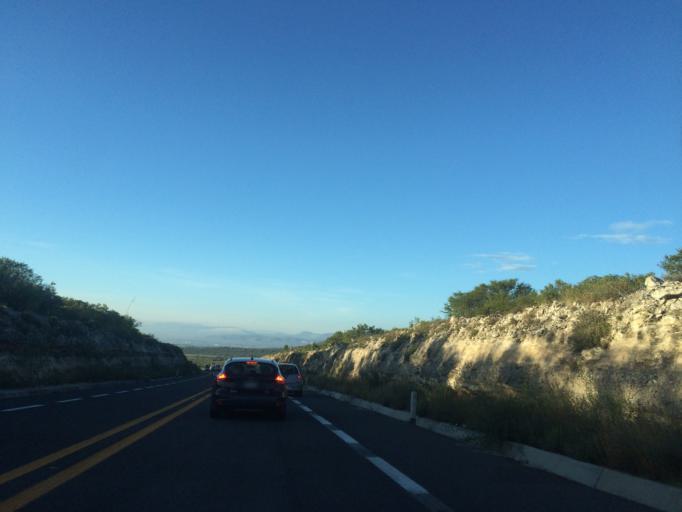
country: MX
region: Puebla
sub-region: Tehuacan
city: Magdalena Cuayucatepec
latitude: 18.6010
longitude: -97.4745
